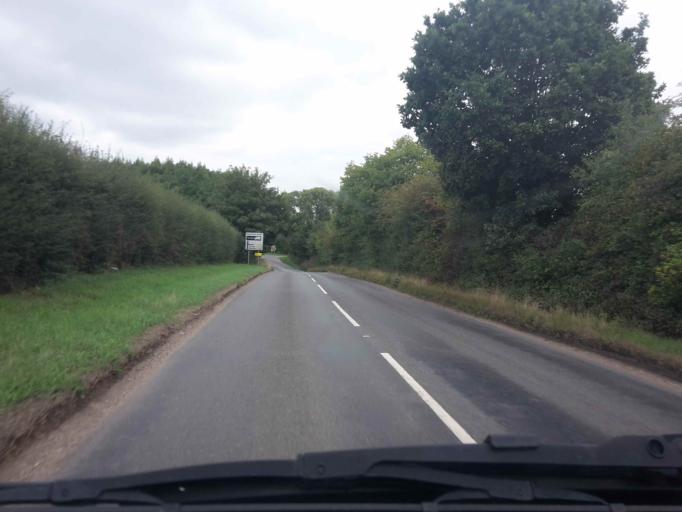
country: GB
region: England
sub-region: Oxfordshire
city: Rotherfield Peppard
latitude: 51.5363
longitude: -0.9761
